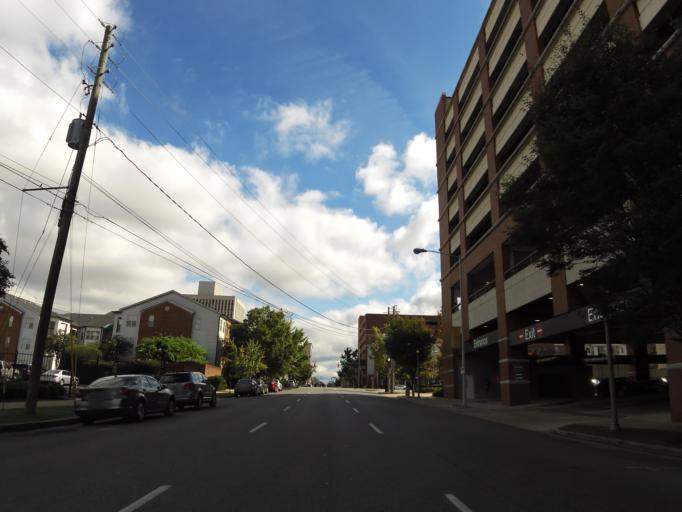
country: US
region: Alabama
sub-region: Jefferson County
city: Birmingham
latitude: 33.5078
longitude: -86.8044
